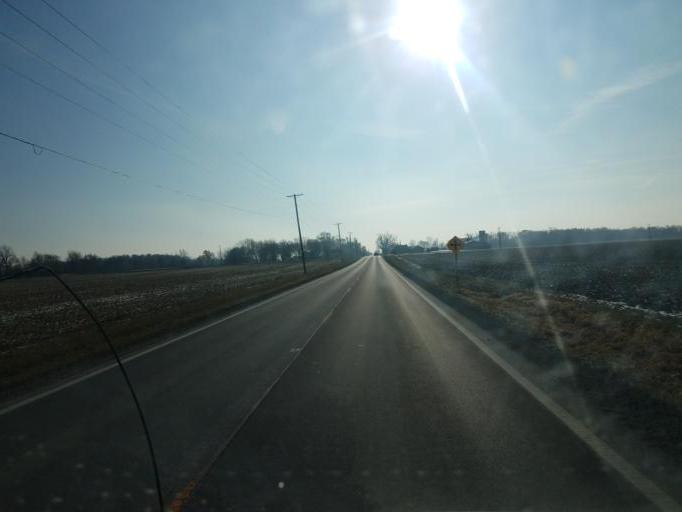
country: US
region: Ohio
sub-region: Marion County
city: Marion
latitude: 40.5663
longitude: -83.0451
